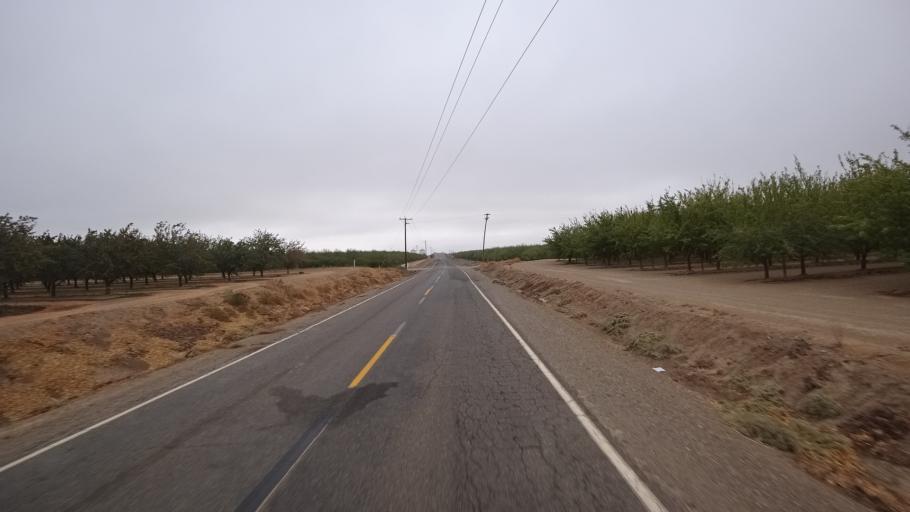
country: US
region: California
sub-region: Yolo County
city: Dunnigan
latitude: 38.9255
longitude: -122.0085
